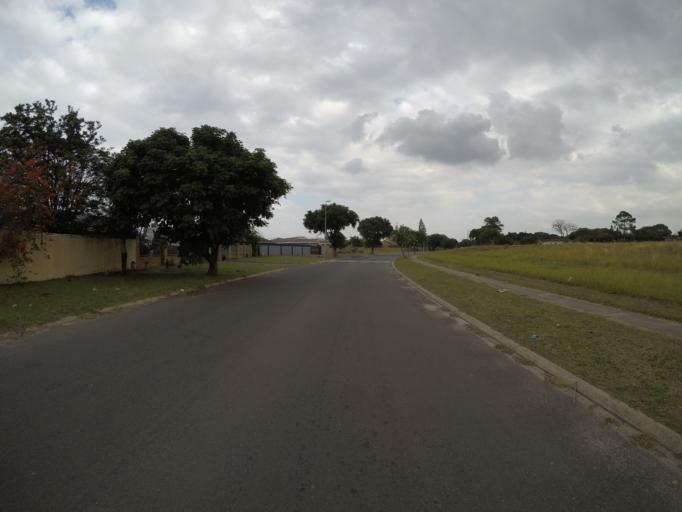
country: ZA
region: KwaZulu-Natal
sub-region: uThungulu District Municipality
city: Richards Bay
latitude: -28.7352
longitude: 32.0497
